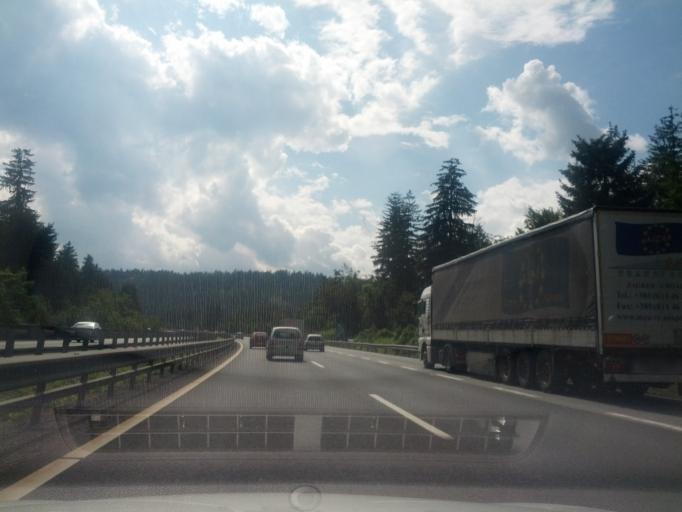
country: SI
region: Vrhnika
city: Vrhnika
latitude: 45.9455
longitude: 14.2864
